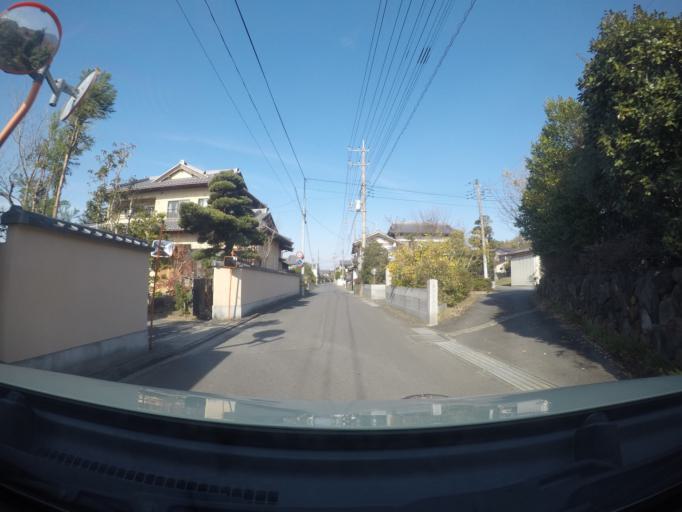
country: JP
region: Ibaraki
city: Tsukuba
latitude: 36.2251
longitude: 140.0656
